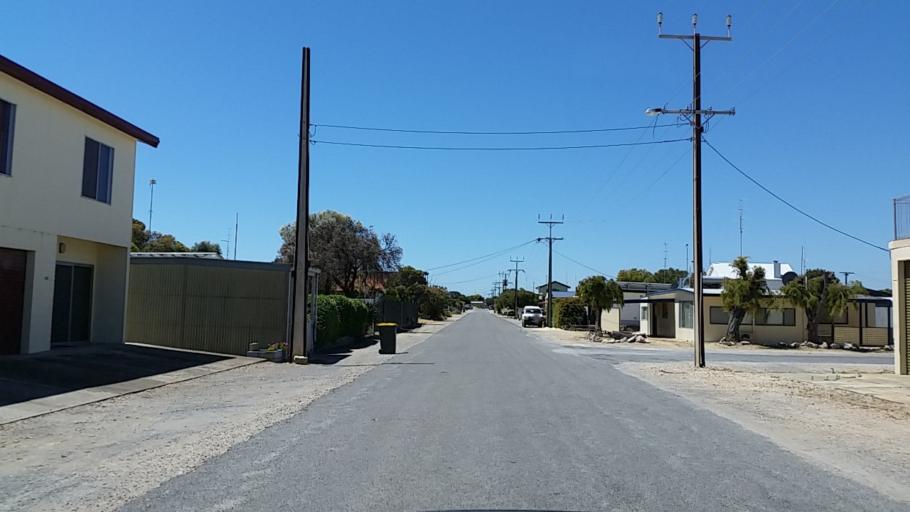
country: AU
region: South Australia
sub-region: Yorke Peninsula
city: Honiton
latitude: -35.2419
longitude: 136.9789
